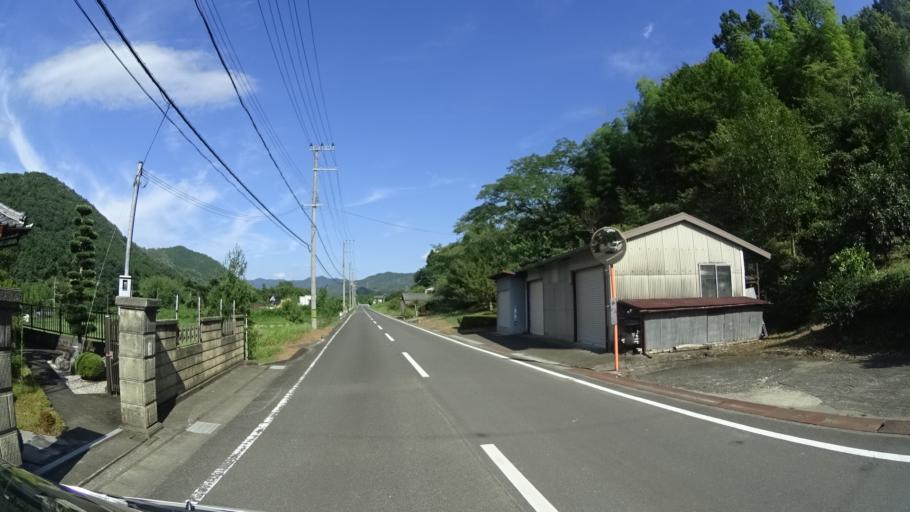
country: JP
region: Kyoto
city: Ayabe
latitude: 35.2882
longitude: 135.2760
